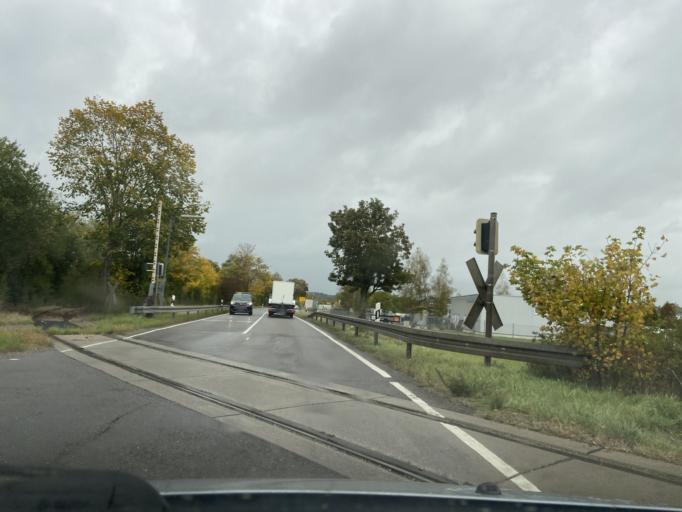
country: DE
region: Baden-Wuerttemberg
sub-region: Tuebingen Region
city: Krauchenwies
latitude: 48.0161
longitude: 9.2352
